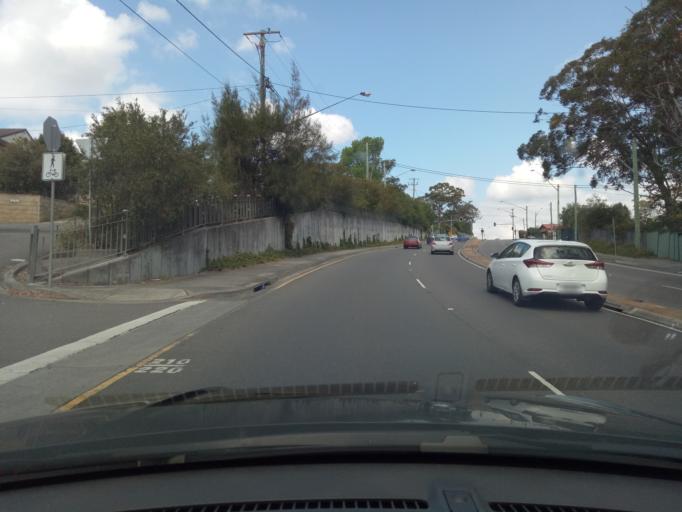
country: AU
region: New South Wales
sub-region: Gosford Shire
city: Erina
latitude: -33.4314
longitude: 151.3920
